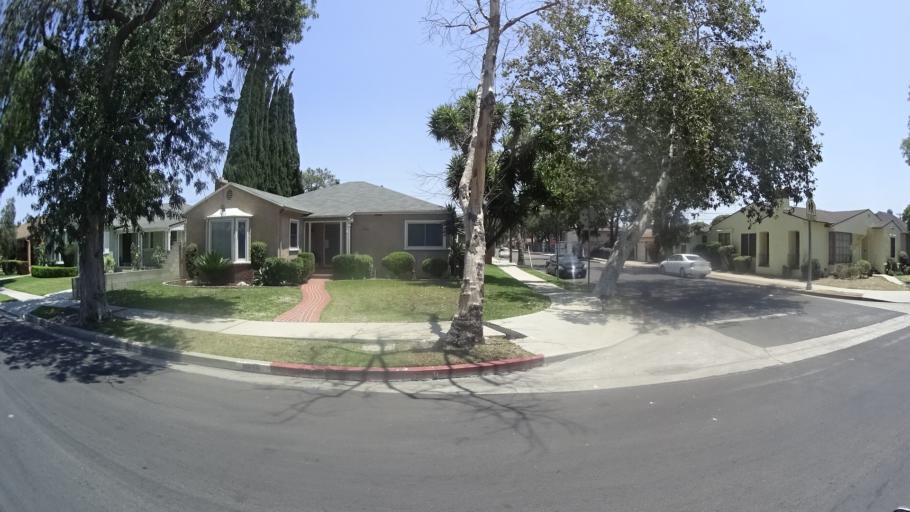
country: US
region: California
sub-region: Los Angeles County
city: View Park-Windsor Hills
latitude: 34.0163
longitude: -118.3242
